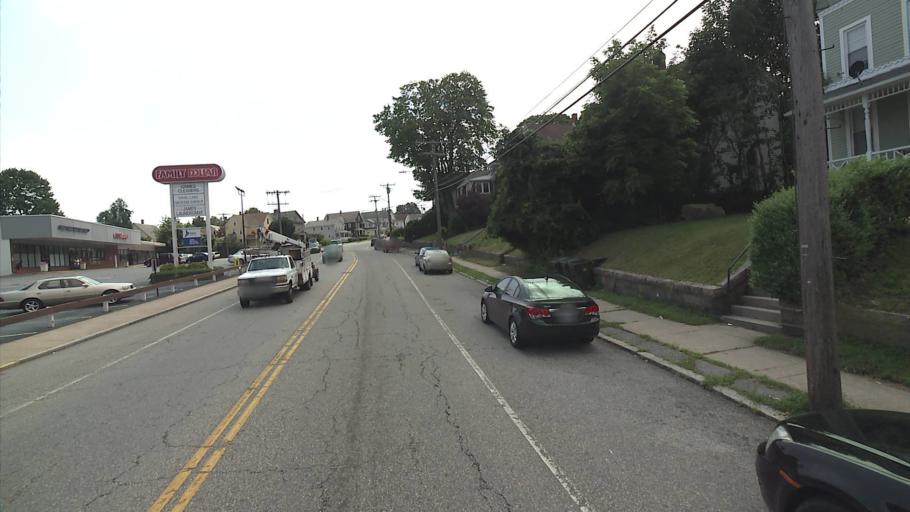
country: US
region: Connecticut
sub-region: New London County
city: New London
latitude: 41.3475
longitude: -72.1071
